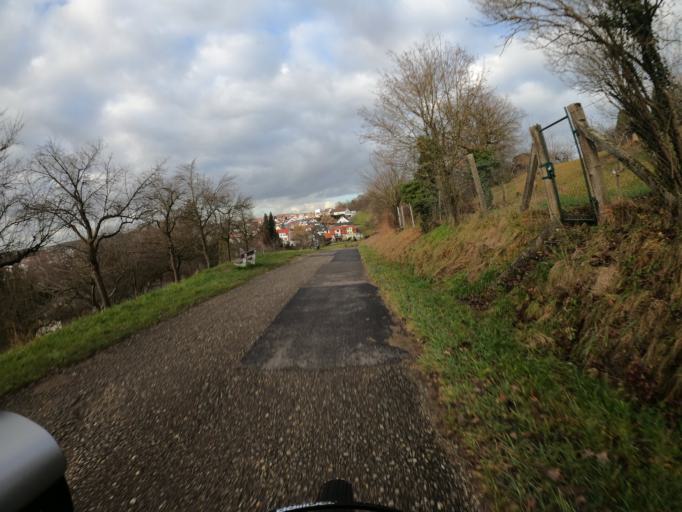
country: DE
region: Baden-Wuerttemberg
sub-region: Regierungsbezirk Stuttgart
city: Wernau
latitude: 48.6857
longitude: 9.4286
